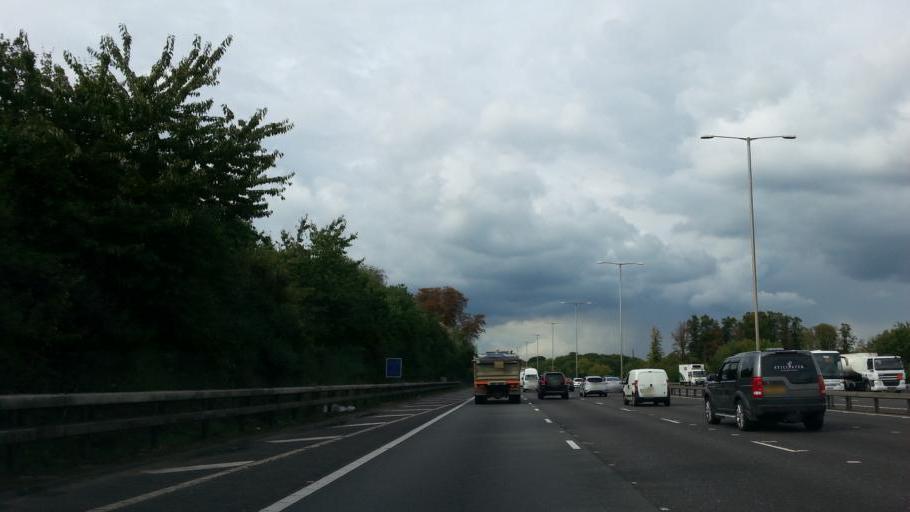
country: GB
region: England
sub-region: Greater London
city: Uxbridge
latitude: 51.5355
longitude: -0.5004
